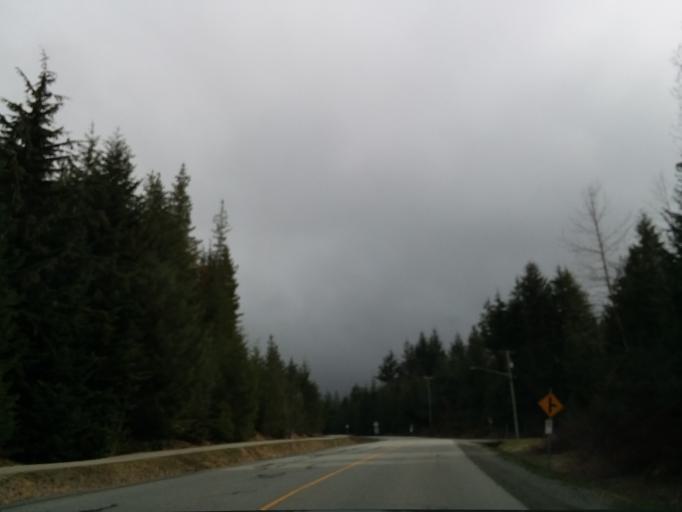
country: CA
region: British Columbia
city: Whistler
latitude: 50.1265
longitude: -122.9626
